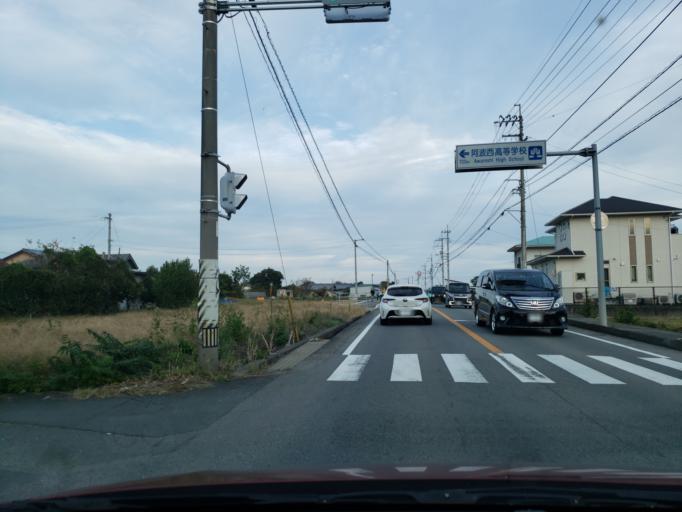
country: JP
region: Tokushima
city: Kamojimacho-jogejima
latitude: 34.0811
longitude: 134.2638
